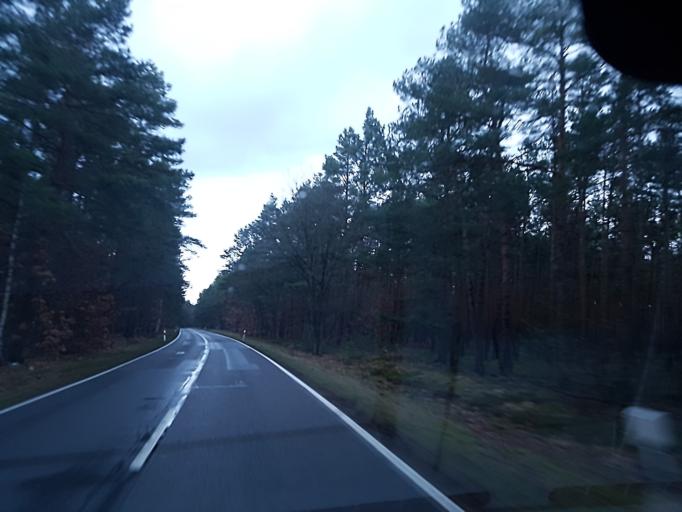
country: DE
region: Brandenburg
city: Finsterwalde
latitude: 51.5493
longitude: 13.6716
